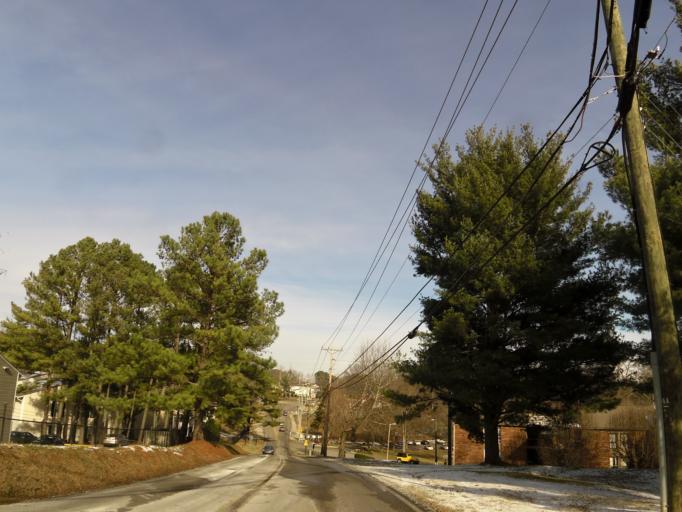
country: US
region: Tennessee
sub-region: Blount County
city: Louisville
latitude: 35.9136
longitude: -84.0613
